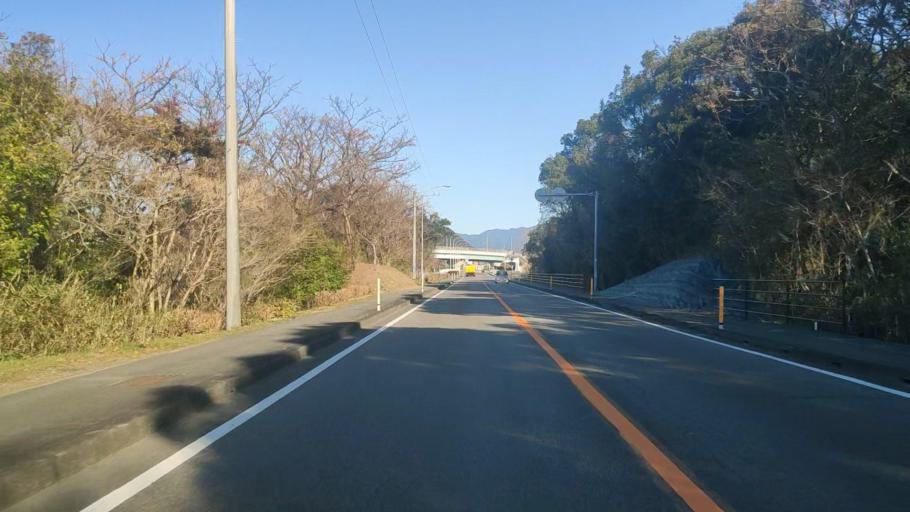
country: JP
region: Miyazaki
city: Nobeoka
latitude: 32.5339
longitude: 131.6802
